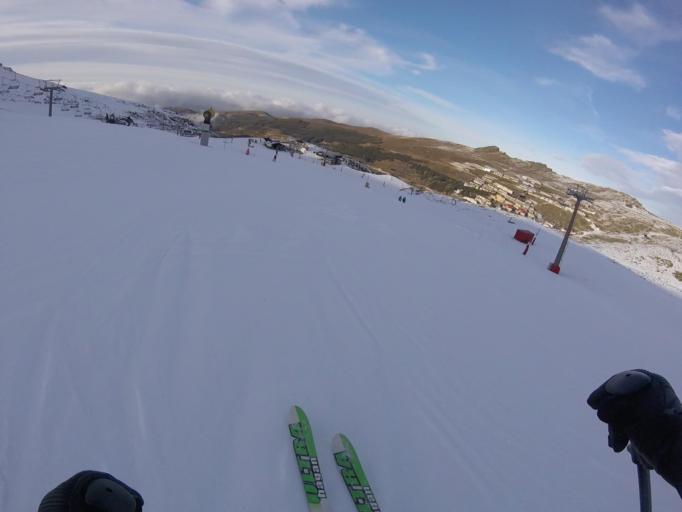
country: ES
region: Andalusia
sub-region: Provincia de Granada
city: Guejar-Sierra
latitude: 37.0811
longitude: -3.4048
